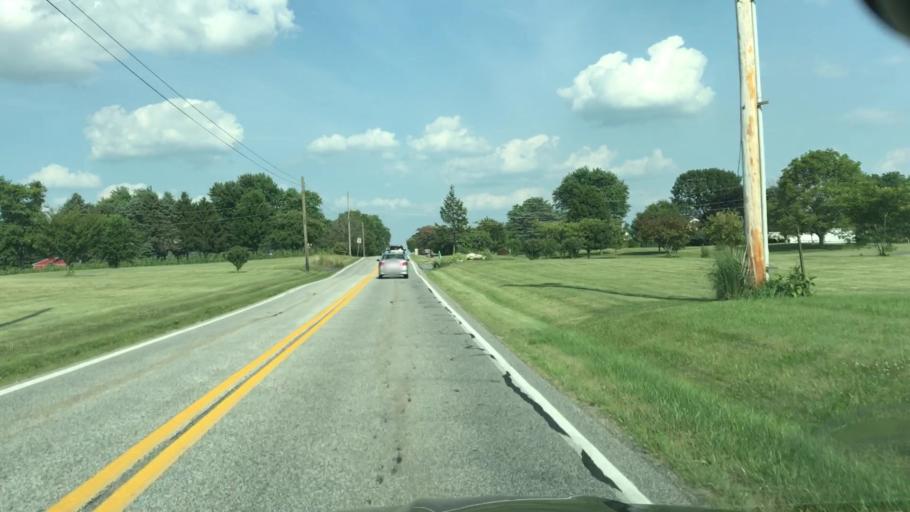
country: US
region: Pennsylvania
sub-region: Cumberland County
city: Boiling Springs
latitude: 40.1814
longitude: -77.0992
